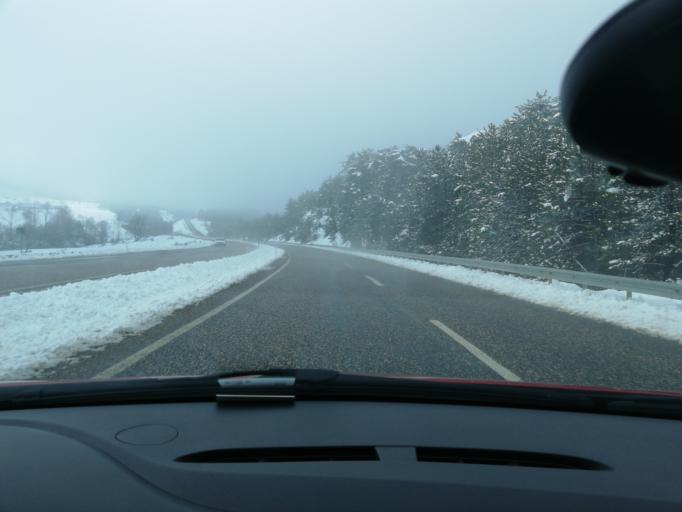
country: TR
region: Kastamonu
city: Akkaya
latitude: 41.2914
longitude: 33.4750
